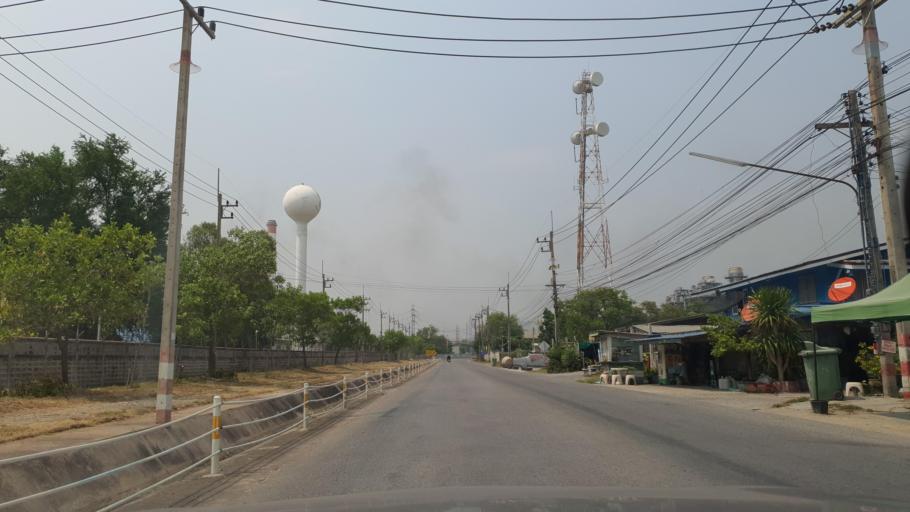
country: TH
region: Chachoengsao
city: Bang Pakong
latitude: 13.4953
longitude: 101.0281
